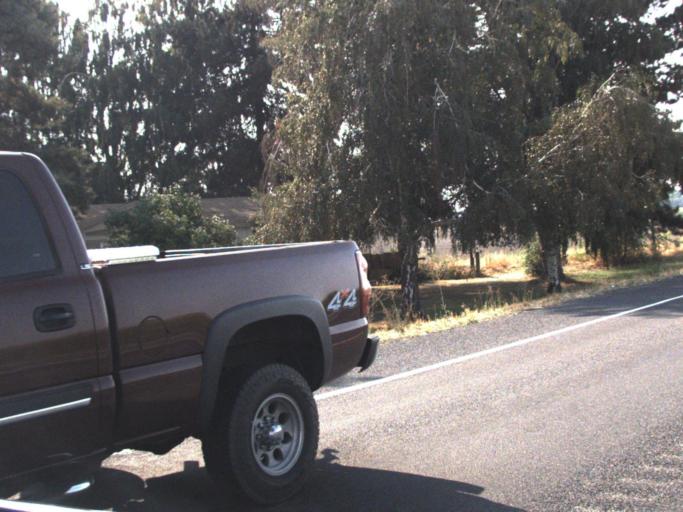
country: US
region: Washington
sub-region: Yakima County
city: Toppenish
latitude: 46.3622
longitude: -120.3040
